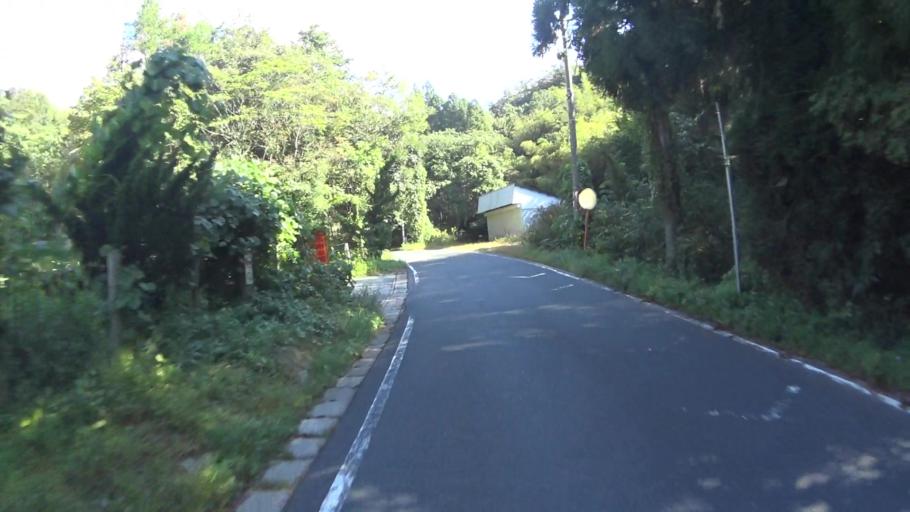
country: JP
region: Kyoto
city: Miyazu
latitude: 35.5826
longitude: 135.1605
